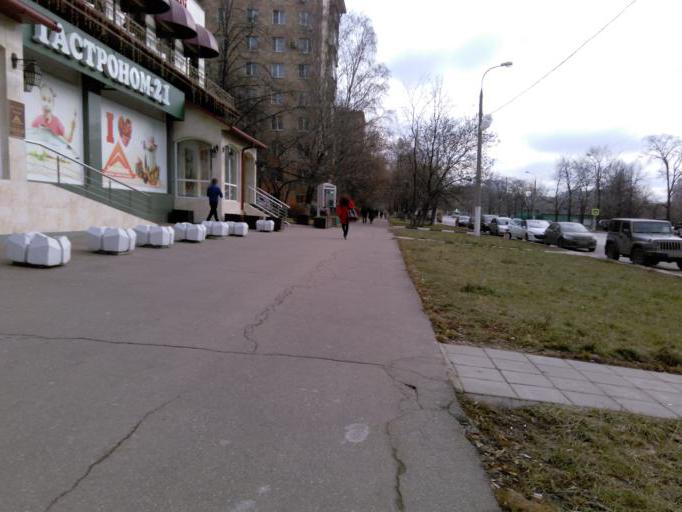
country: RU
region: Moscow
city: Ramenki
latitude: 55.6776
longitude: 37.5163
